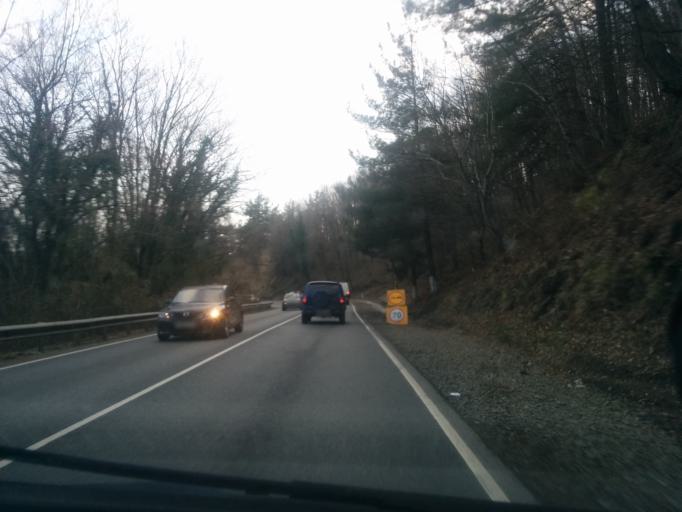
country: RU
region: Krasnodarskiy
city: Agoy
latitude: 44.1297
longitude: 39.0462
